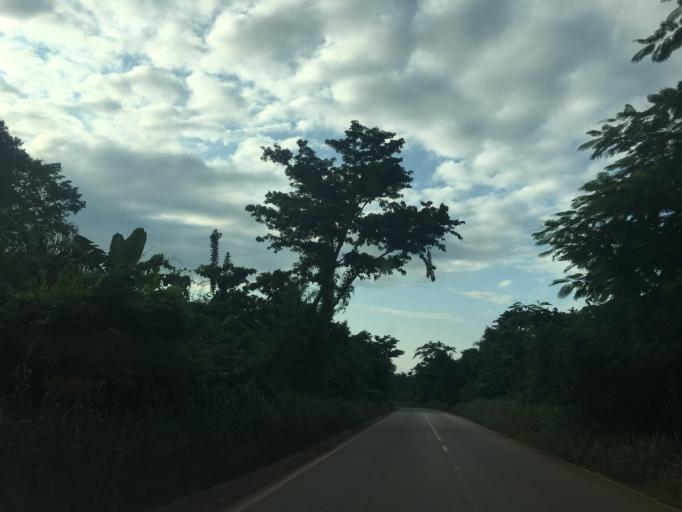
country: GH
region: Western
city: Bibiani
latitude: 6.4094
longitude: -2.3009
